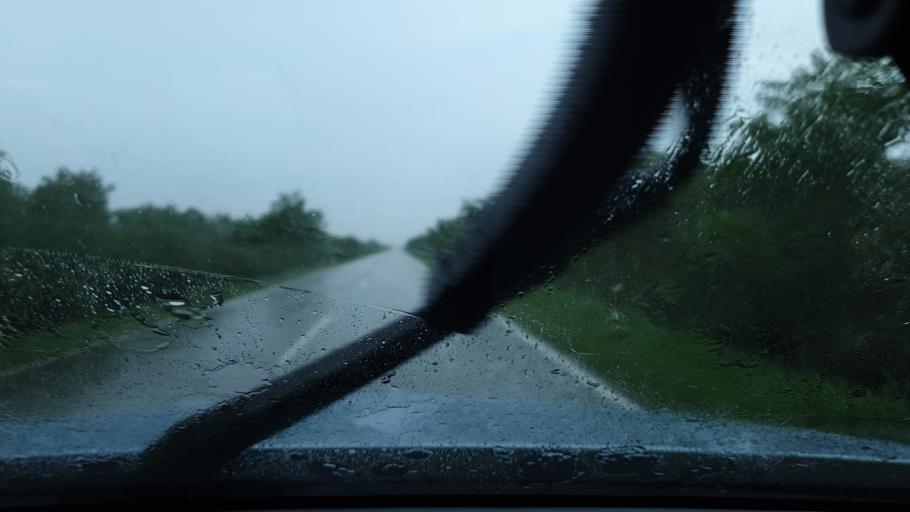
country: RS
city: Lazarevo
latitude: 45.3887
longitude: 20.5974
